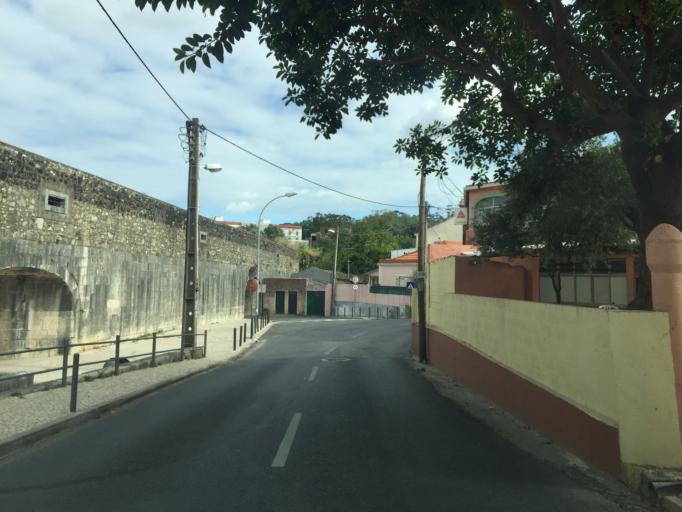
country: PT
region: Lisbon
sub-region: Odivelas
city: Pontinha
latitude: 38.7423
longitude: -9.2035
